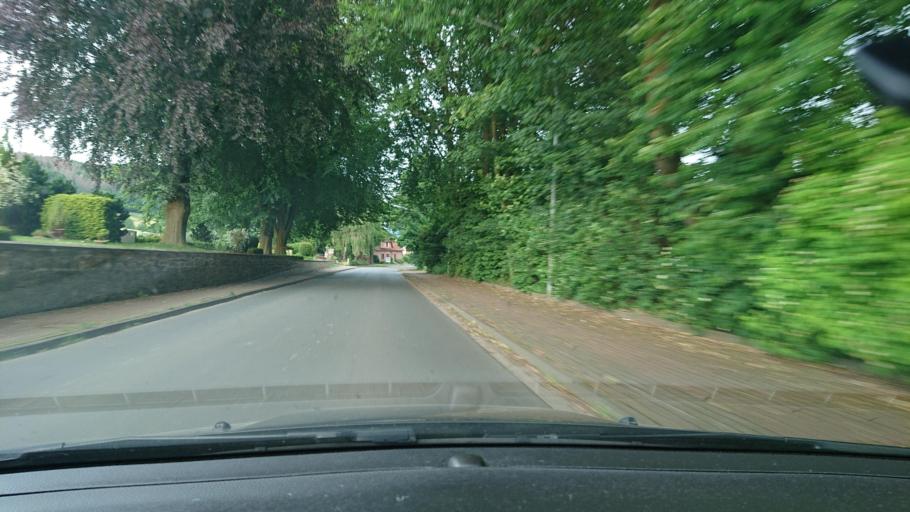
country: DE
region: North Rhine-Westphalia
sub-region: Regierungsbezirk Detmold
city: Rodinghausen
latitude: 52.2765
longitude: 8.4920
